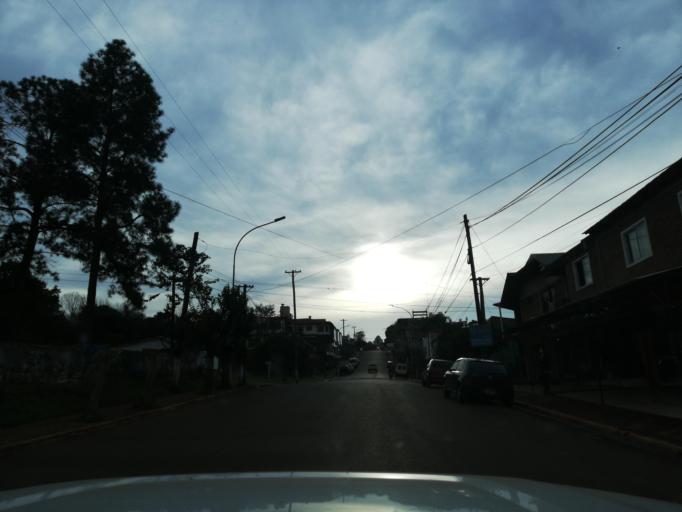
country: AR
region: Misiones
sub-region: Departamento de San Pedro
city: San Pedro
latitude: -26.6221
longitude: -54.1094
